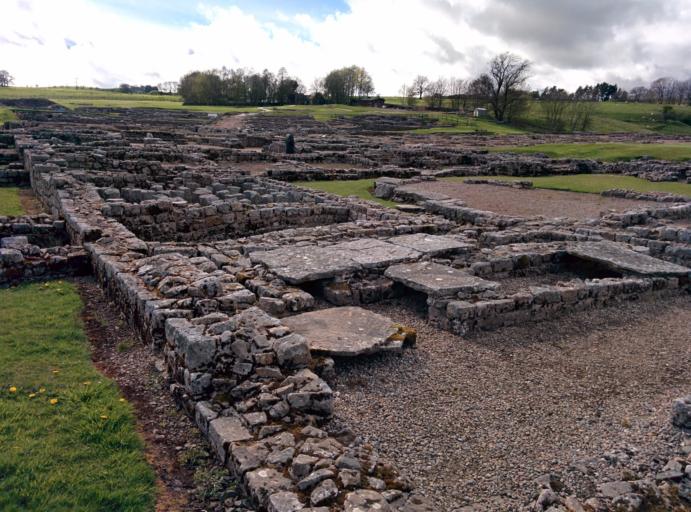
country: GB
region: England
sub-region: Northumberland
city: Bardon Mill
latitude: 54.9911
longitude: -2.3596
